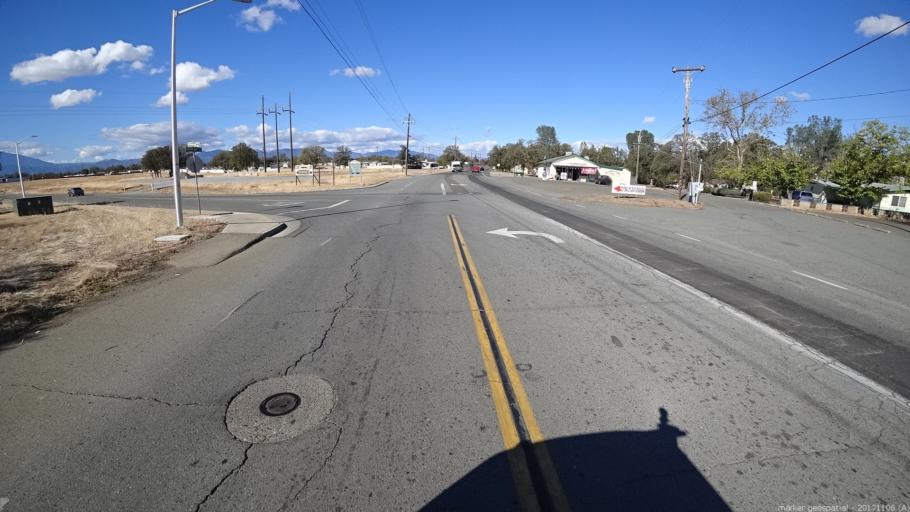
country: US
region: California
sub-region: Shasta County
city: Palo Cedro
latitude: 40.5781
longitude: -122.3054
